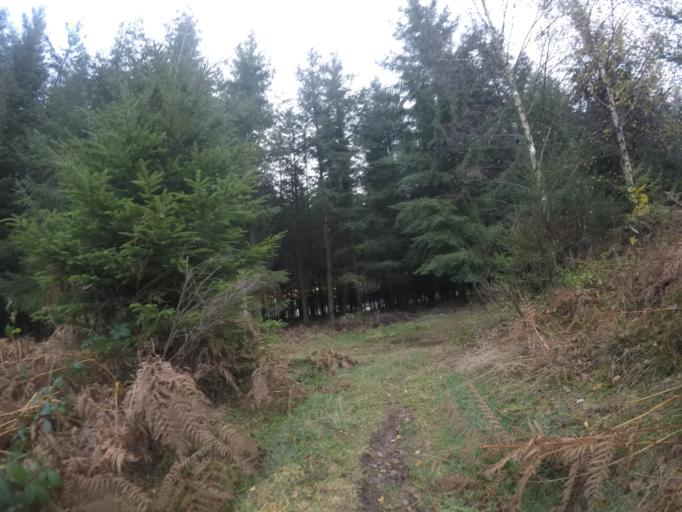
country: BE
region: Wallonia
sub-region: Province du Luxembourg
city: Habay-la-Vieille
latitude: 49.7409
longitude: 5.6052
